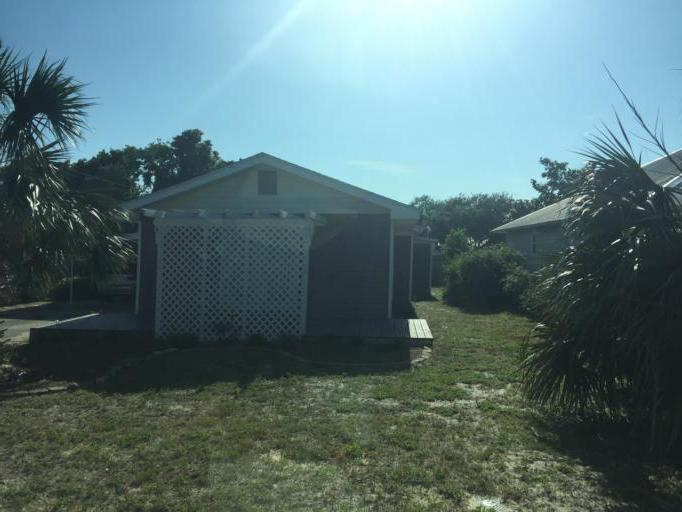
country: US
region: Florida
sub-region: Bay County
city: Panama City Beach
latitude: 30.1977
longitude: -85.8399
